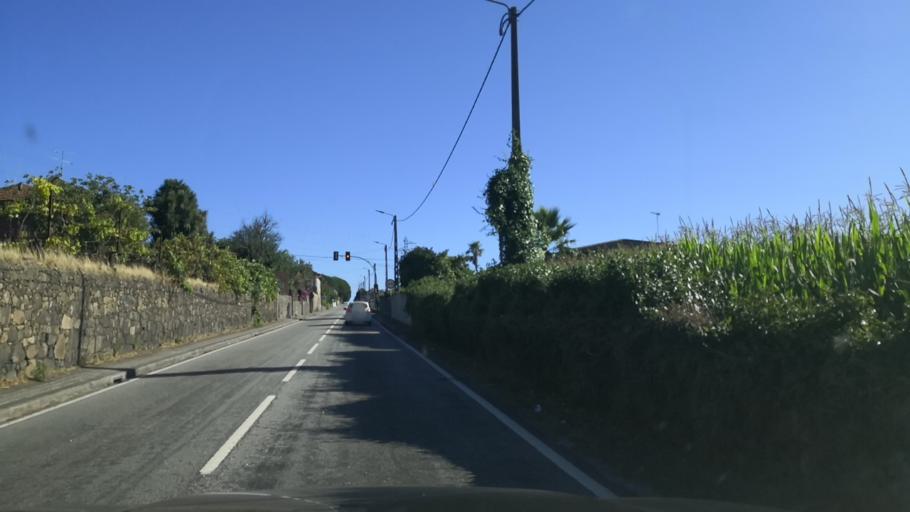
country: PT
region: Porto
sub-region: Santo Tirso
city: Sao Miguel do Couto
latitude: 41.3017
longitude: -8.4710
